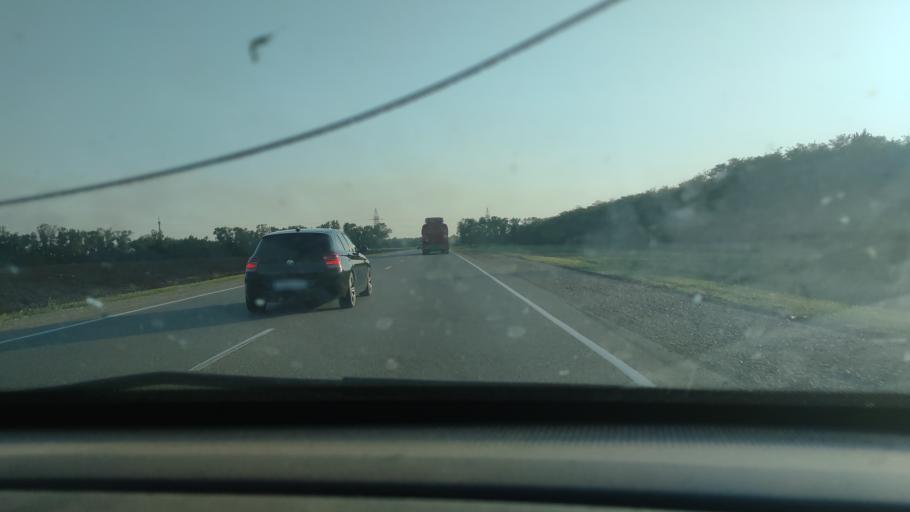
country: RU
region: Krasnodarskiy
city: Kanevskaya
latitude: 46.0351
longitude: 38.9797
